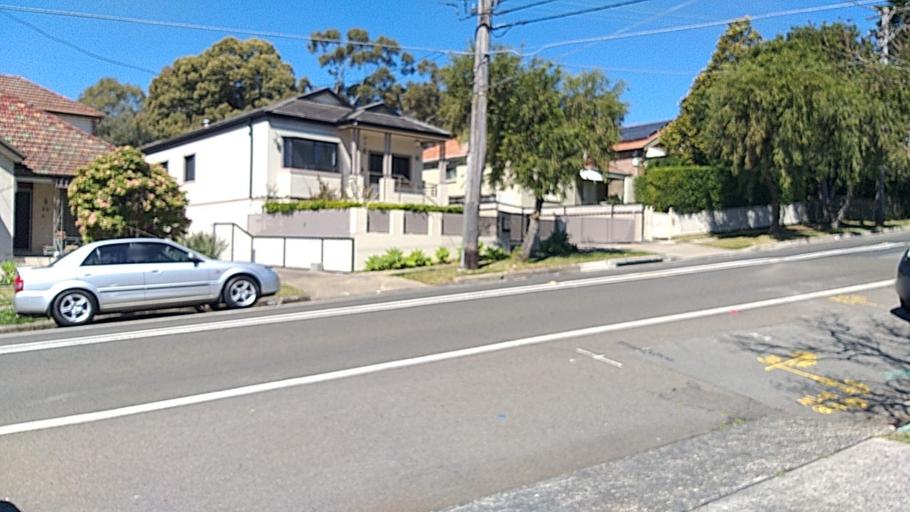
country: AU
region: New South Wales
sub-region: Ryde
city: East Ryde
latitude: -33.8209
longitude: 151.1266
